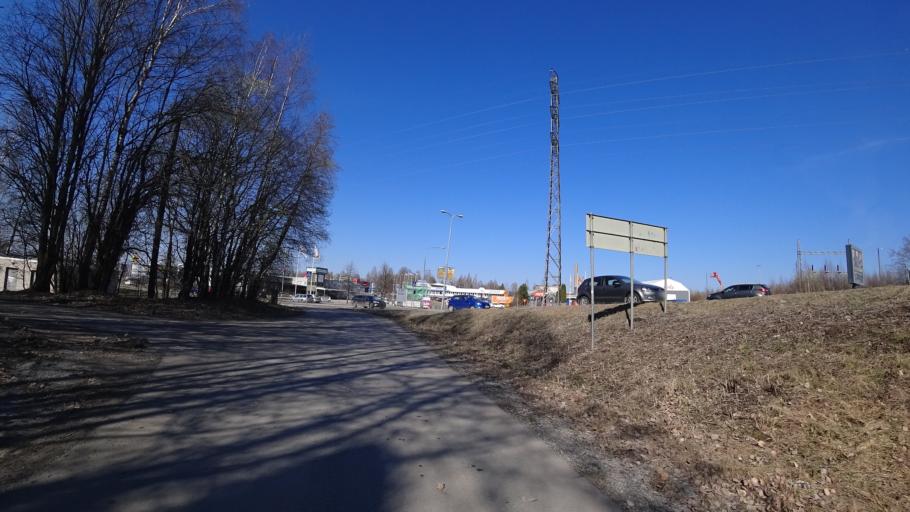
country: FI
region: Pirkanmaa
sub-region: Tampere
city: Pirkkala
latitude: 61.5124
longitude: 23.6770
